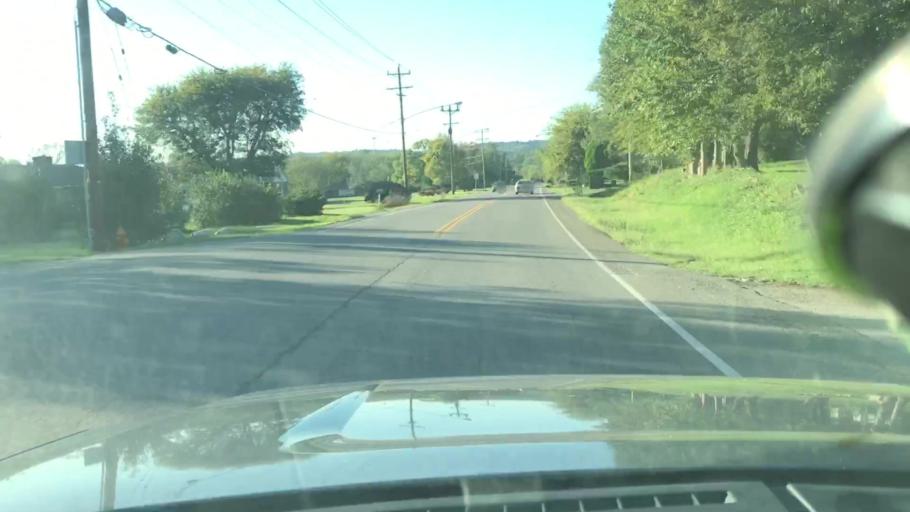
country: US
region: Tennessee
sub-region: Davidson County
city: Nashville
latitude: 36.1997
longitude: -86.8465
